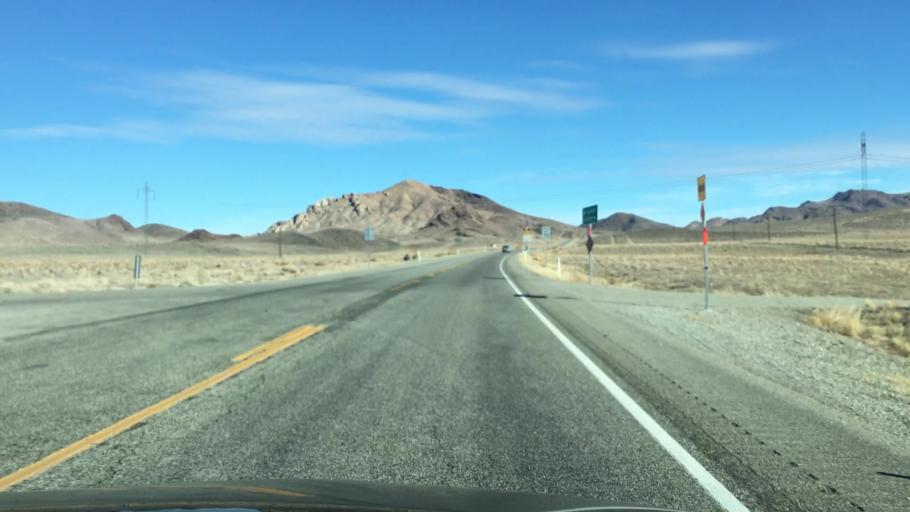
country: US
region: Nevada
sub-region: Lyon County
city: Yerington
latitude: 39.0308
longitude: -119.0352
